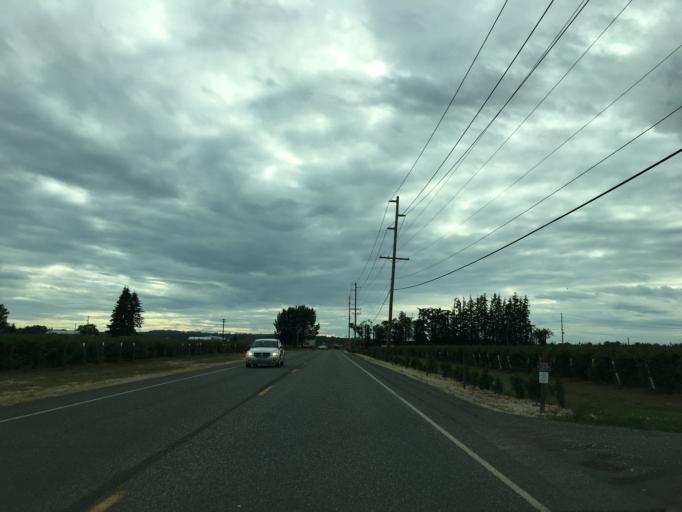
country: US
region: Washington
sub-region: Whatcom County
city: Ferndale
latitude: 48.8880
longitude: -122.5369
